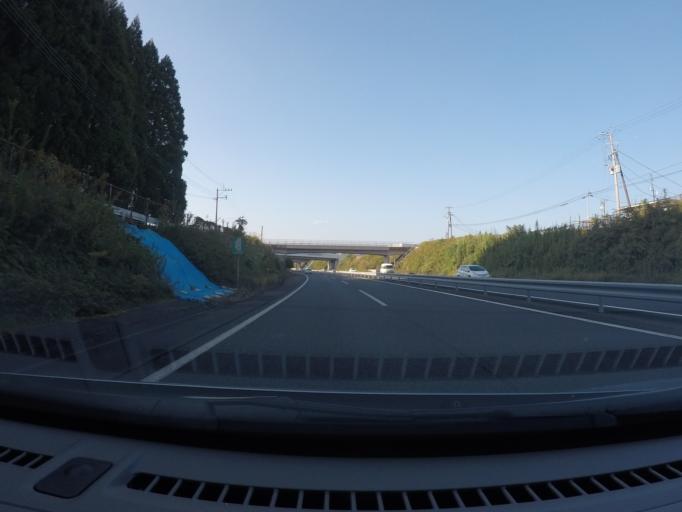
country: JP
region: Kagoshima
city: Kajiki
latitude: 31.8141
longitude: 130.7067
